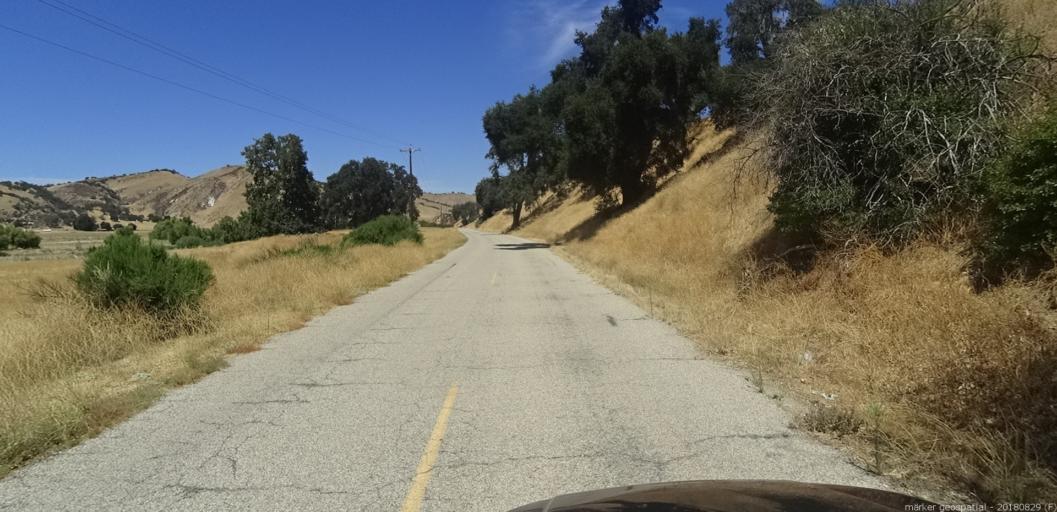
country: US
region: California
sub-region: San Luis Obispo County
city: Lake Nacimiento
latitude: 35.7993
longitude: -120.8562
